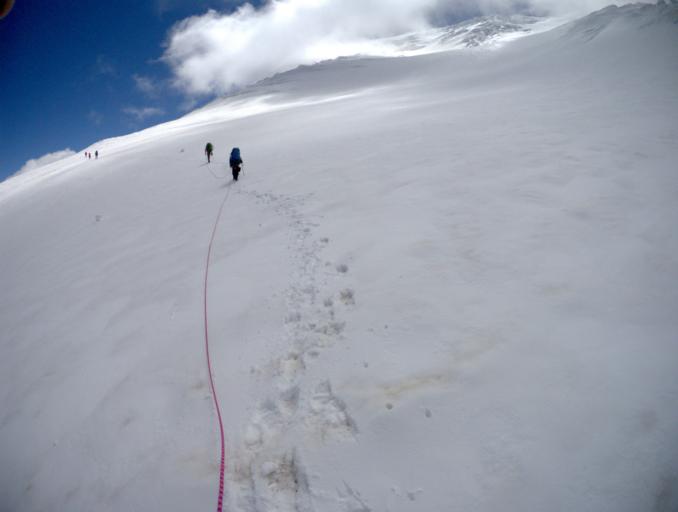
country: RU
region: Kabardino-Balkariya
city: Terskol
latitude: 43.3798
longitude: 42.4494
